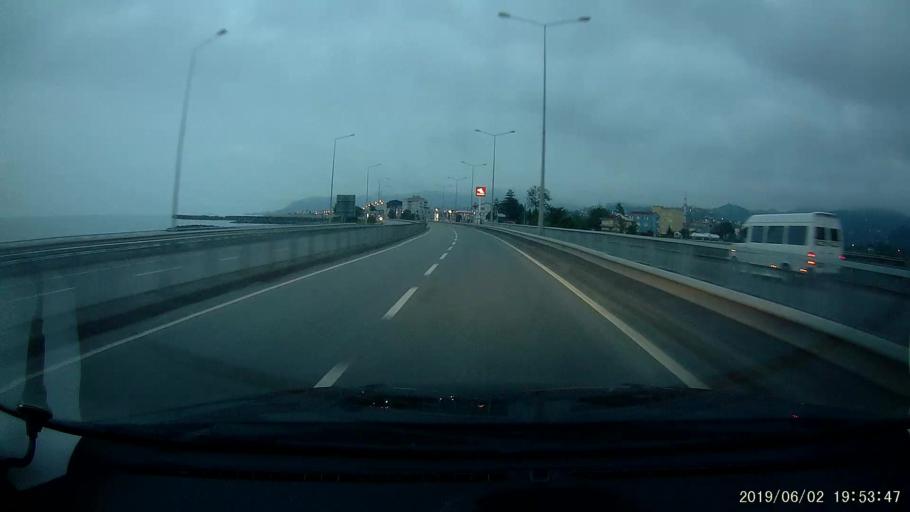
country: TR
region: Trabzon
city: Espiye
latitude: 40.9506
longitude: 38.7140
